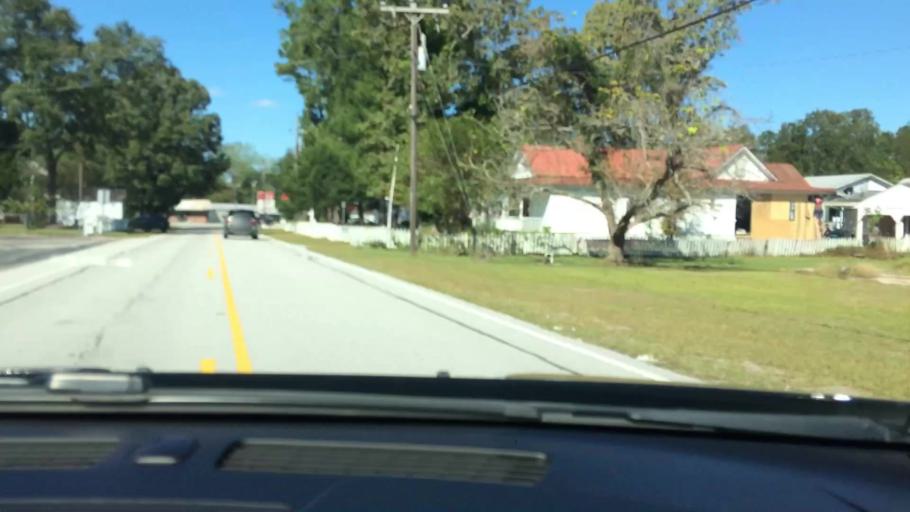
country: US
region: North Carolina
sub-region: Pitt County
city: Grifton
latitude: 35.2907
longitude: -77.3350
